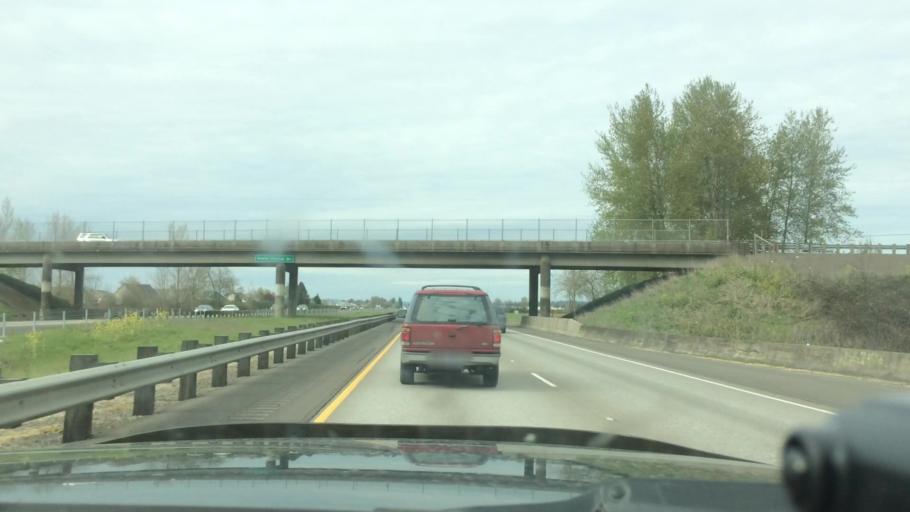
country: US
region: Oregon
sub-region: Linn County
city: Albany
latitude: 44.6104
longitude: -123.0619
